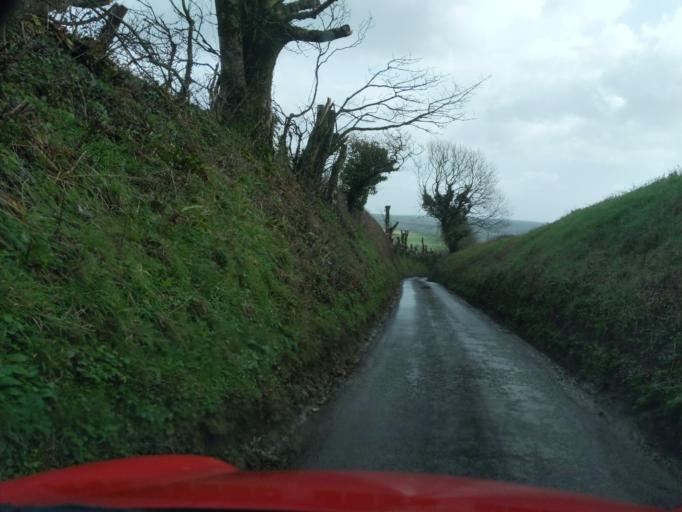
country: GB
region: England
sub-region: Devon
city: Ivybridge
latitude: 50.3641
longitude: -3.9314
